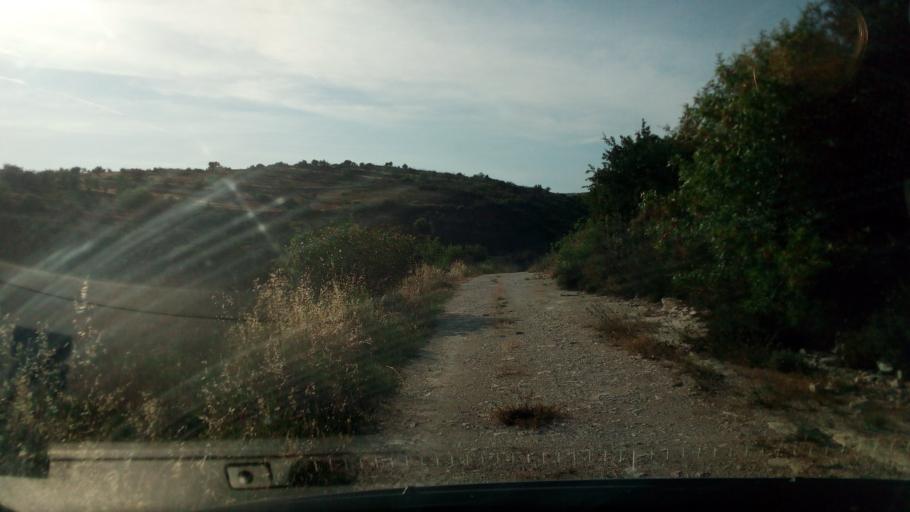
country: CY
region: Pafos
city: Tala
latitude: 34.8720
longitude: 32.4653
